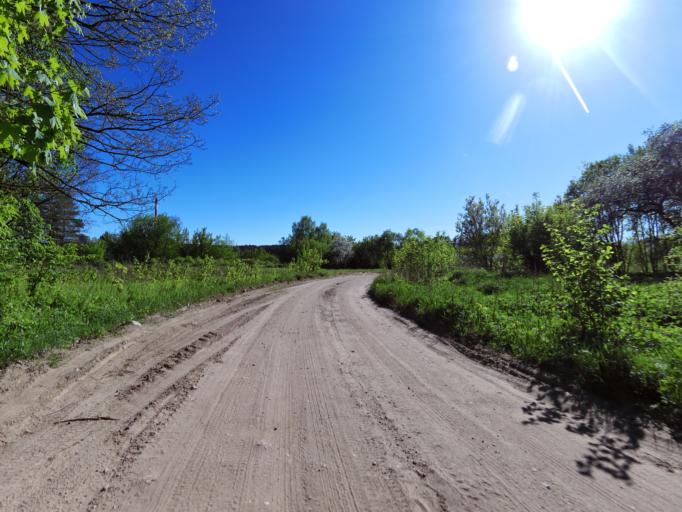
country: LT
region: Vilnius County
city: Pilaite
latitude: 54.6825
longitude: 25.1564
